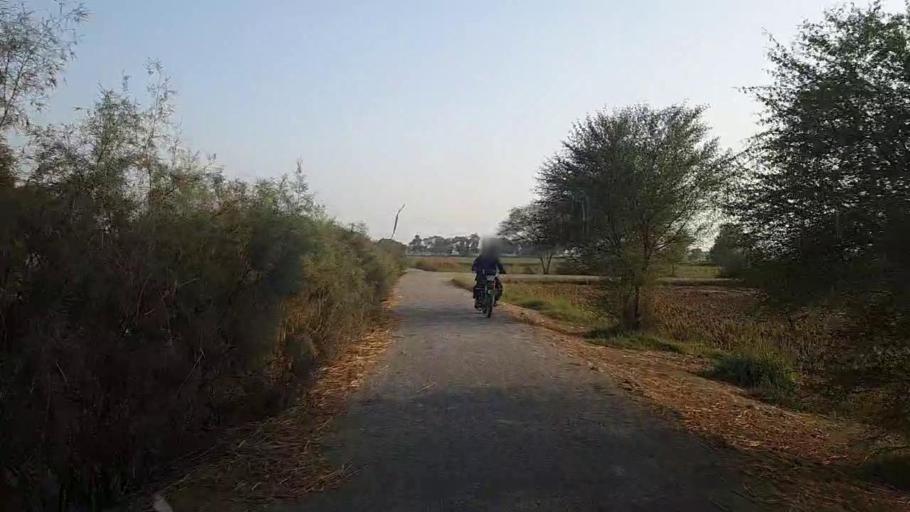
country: PK
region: Sindh
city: Kandhkot
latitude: 28.2360
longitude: 69.0912
